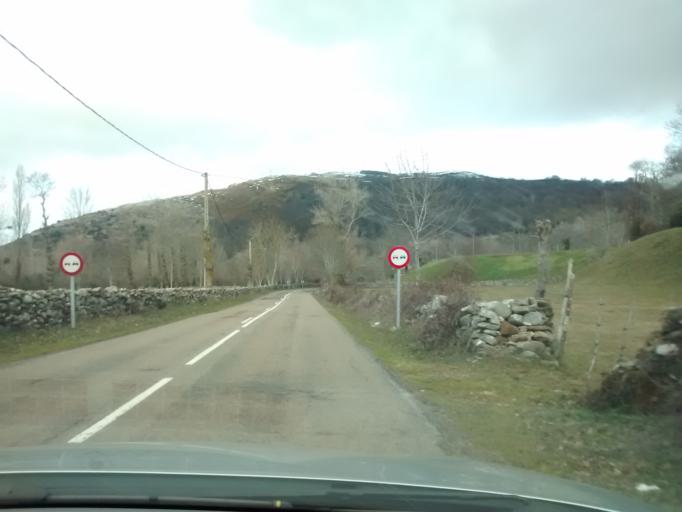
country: ES
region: Castille and Leon
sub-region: Provincia de Burgos
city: Espinosa de los Monteros
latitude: 43.1141
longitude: -3.5810
